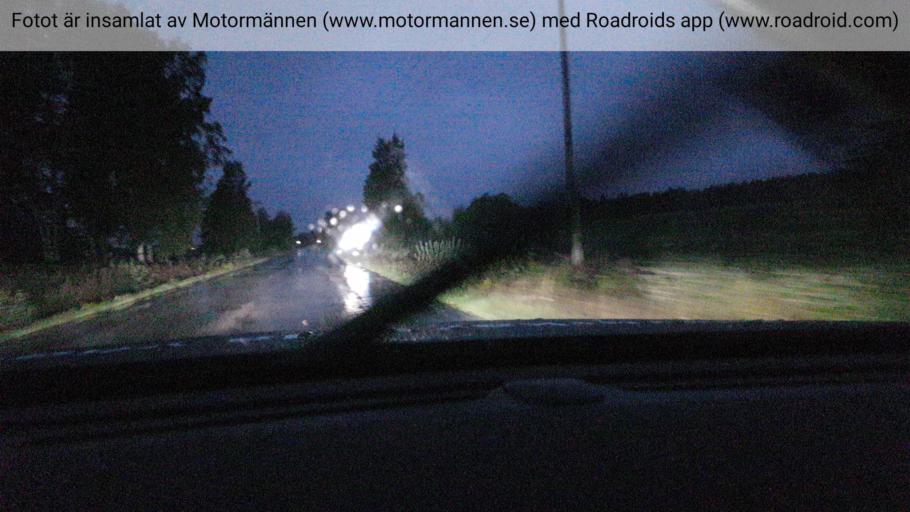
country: SE
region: Vaestra Goetaland
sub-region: Falkopings Kommun
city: Akarp
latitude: 58.2639
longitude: 13.7560
